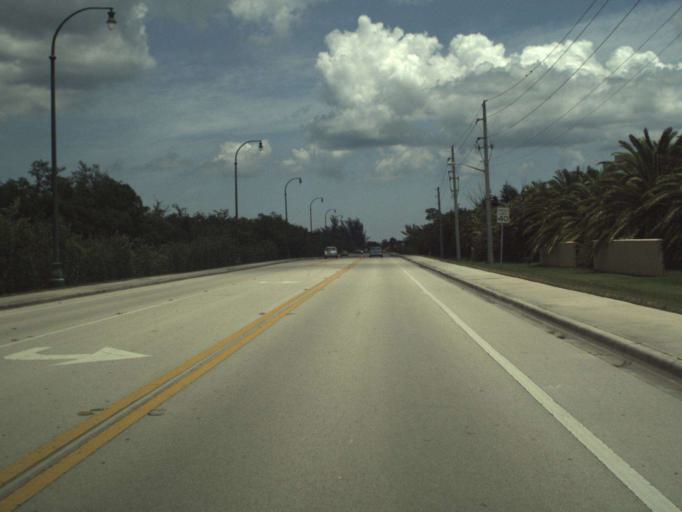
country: US
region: Florida
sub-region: Martin County
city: Jensen Beach
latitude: 27.2557
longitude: -80.2052
